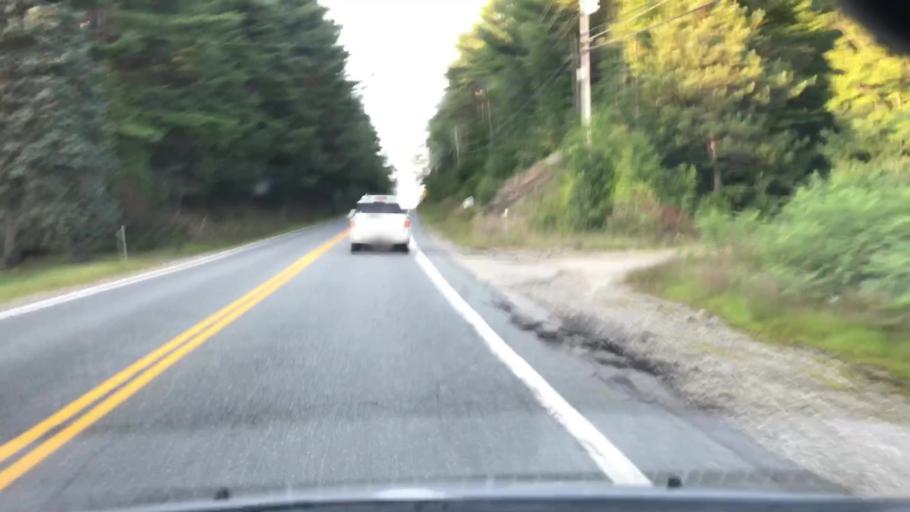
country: US
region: New Hampshire
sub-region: Grafton County
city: Rumney
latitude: 43.8809
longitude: -71.9098
